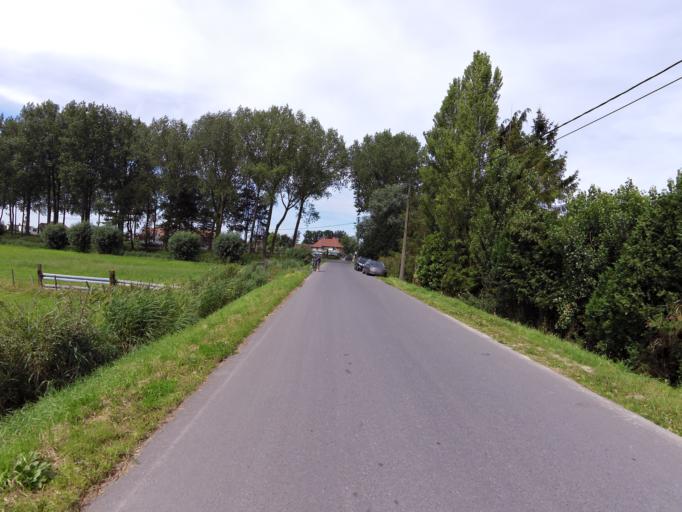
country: NL
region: Zeeland
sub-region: Gemeente Sluis
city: Sluis
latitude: 51.2907
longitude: 3.3380
